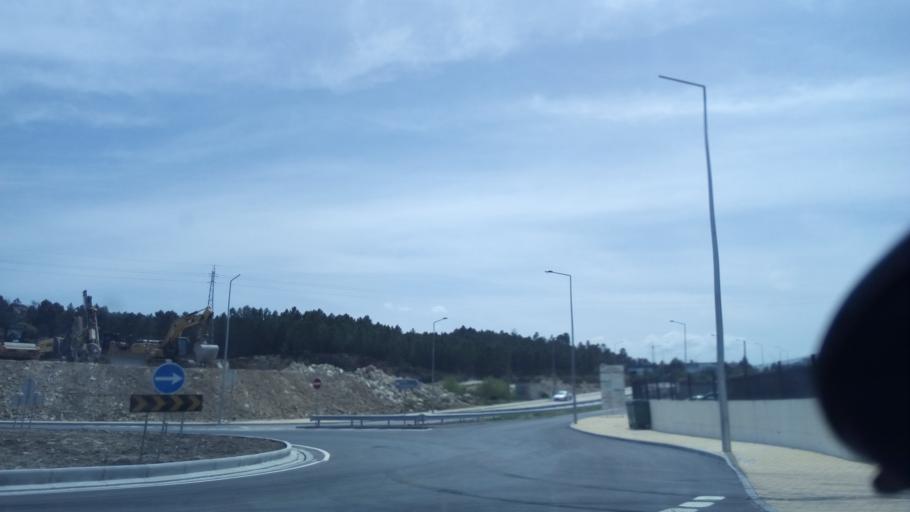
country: PT
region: Viseu
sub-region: Mangualde
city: Mangualde
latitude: 40.6088
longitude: -7.7893
